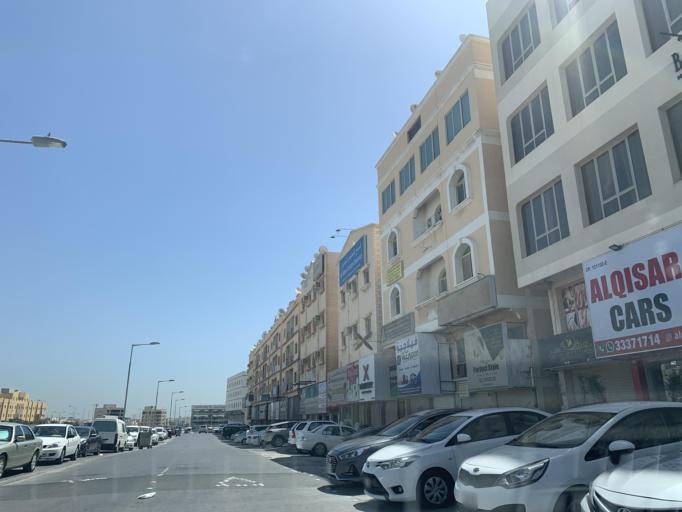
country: BH
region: Northern
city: Ar Rifa'
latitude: 26.1385
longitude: 50.5765
